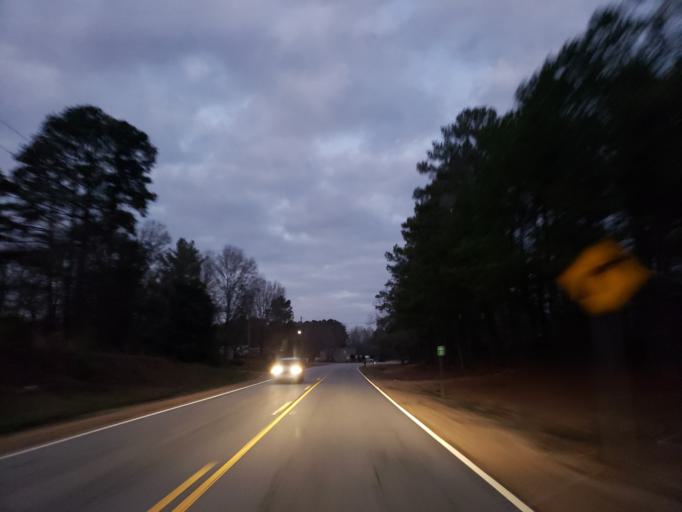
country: US
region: Georgia
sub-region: Carroll County
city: Temple
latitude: 33.8038
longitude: -85.0562
